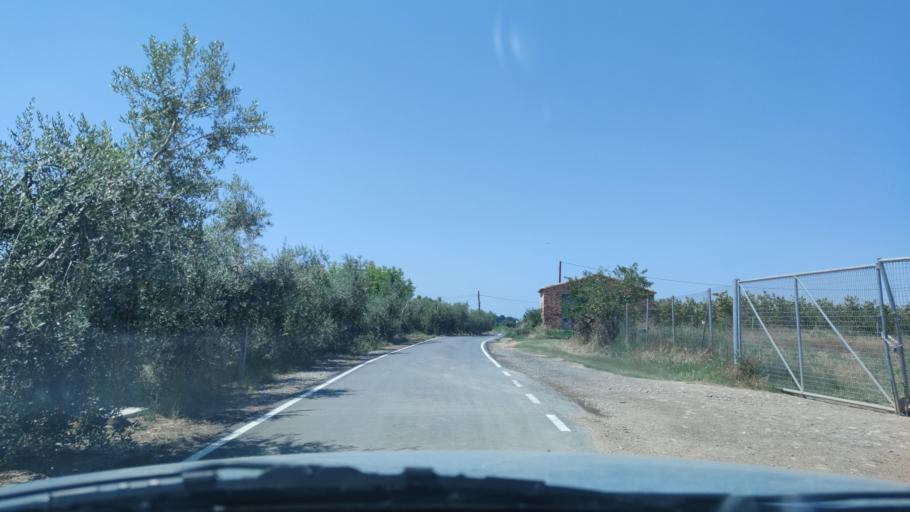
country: ES
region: Catalonia
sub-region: Provincia de Lleida
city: Alpicat
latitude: 41.6584
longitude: 0.5711
